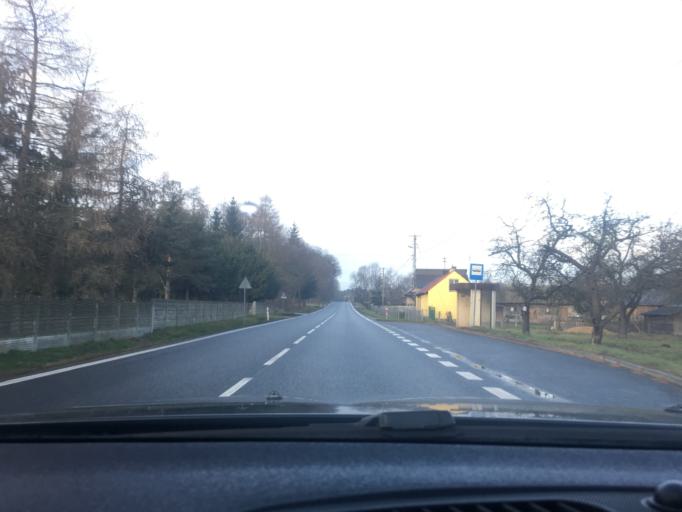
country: PL
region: Swietokrzyskie
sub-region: Powiat jedrzejowski
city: Imielno
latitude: 50.6222
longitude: 20.3986
